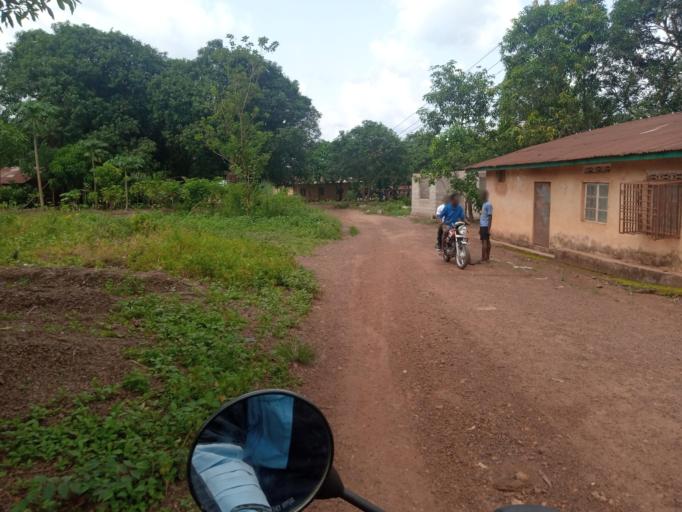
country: SL
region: Southern Province
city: Baoma
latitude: 7.9832
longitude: -11.7273
